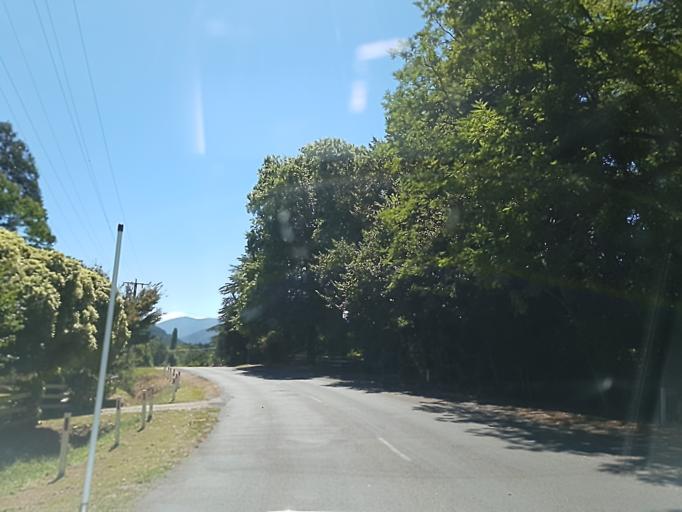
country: AU
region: Victoria
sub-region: Alpine
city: Mount Beauty
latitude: -36.7689
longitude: 146.9817
